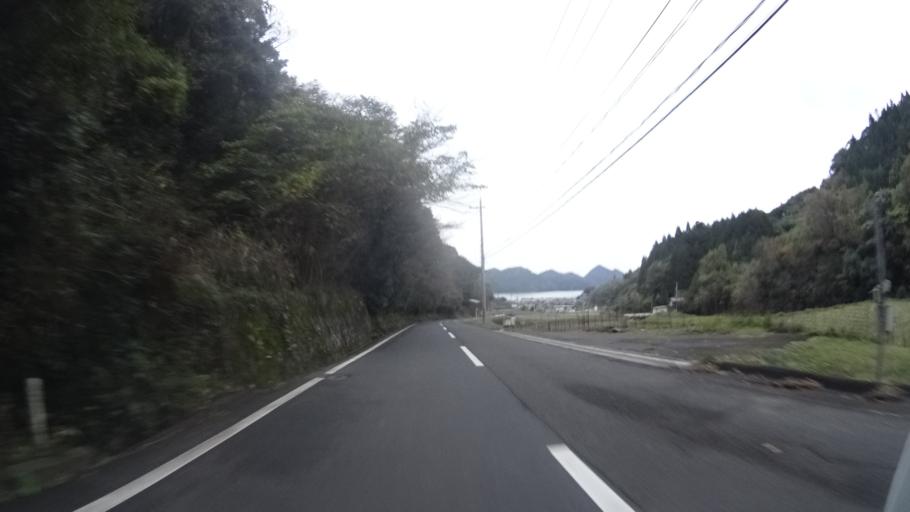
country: JP
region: Kyoto
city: Maizuru
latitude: 35.5610
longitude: 135.4545
